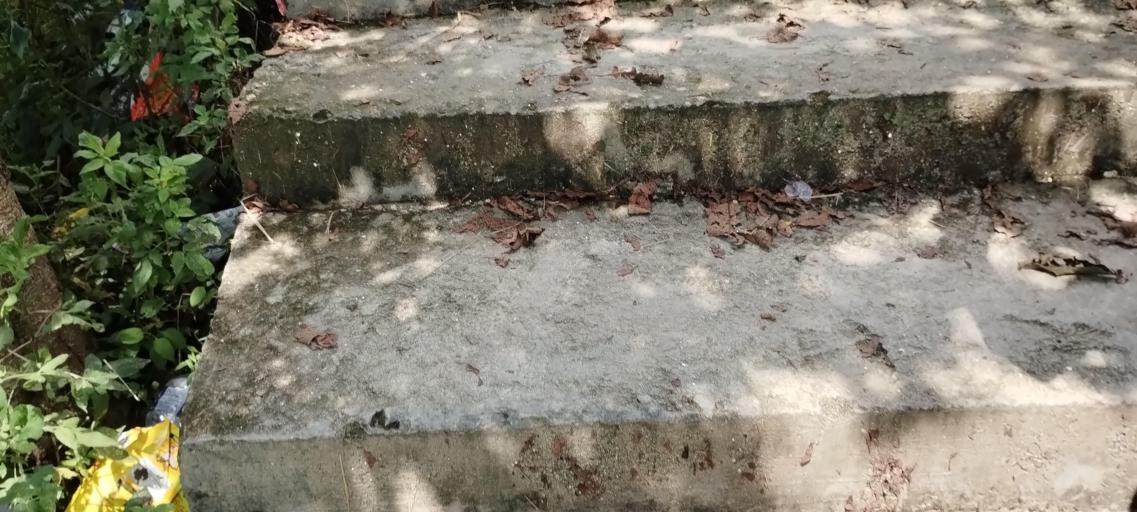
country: NP
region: Central Region
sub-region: Bagmati Zone
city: Kathmandu
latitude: 27.7893
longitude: 85.3609
